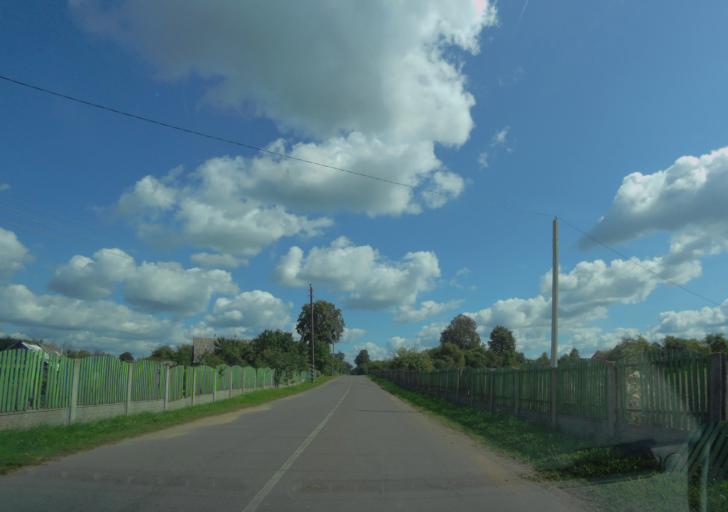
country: BY
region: Minsk
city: Zyembin
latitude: 54.4253
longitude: 28.4220
